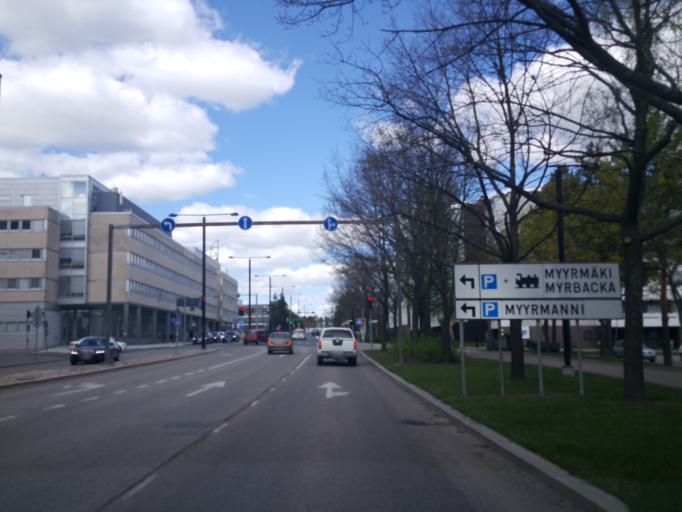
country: FI
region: Uusimaa
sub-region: Helsinki
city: Teekkarikylae
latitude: 60.2595
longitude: 24.8568
